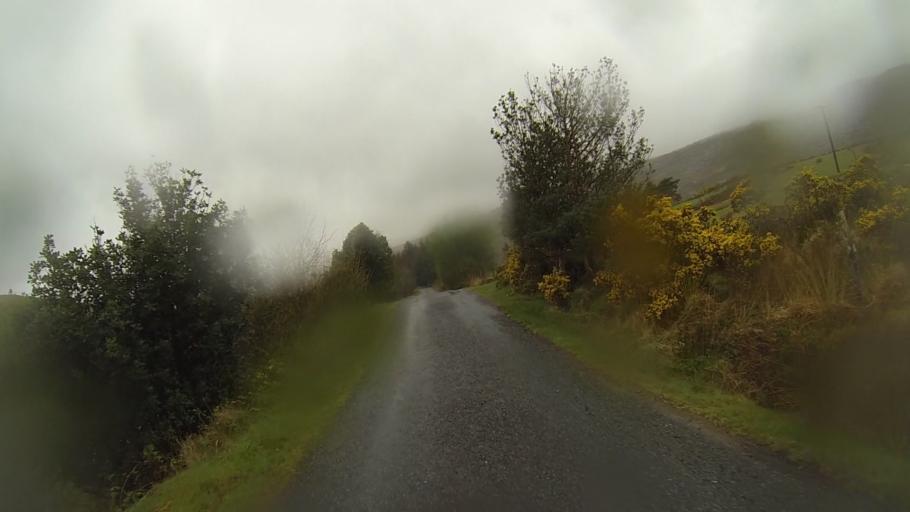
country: IE
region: Munster
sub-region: Ciarrai
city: Kenmare
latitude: 51.9491
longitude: -9.6753
